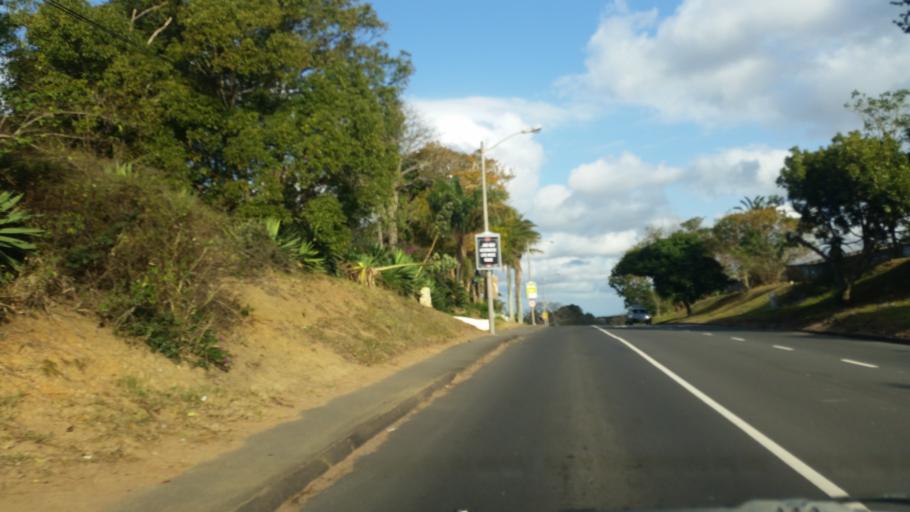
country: ZA
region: KwaZulu-Natal
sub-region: eThekwini Metropolitan Municipality
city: Berea
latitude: -29.8403
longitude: 30.9264
